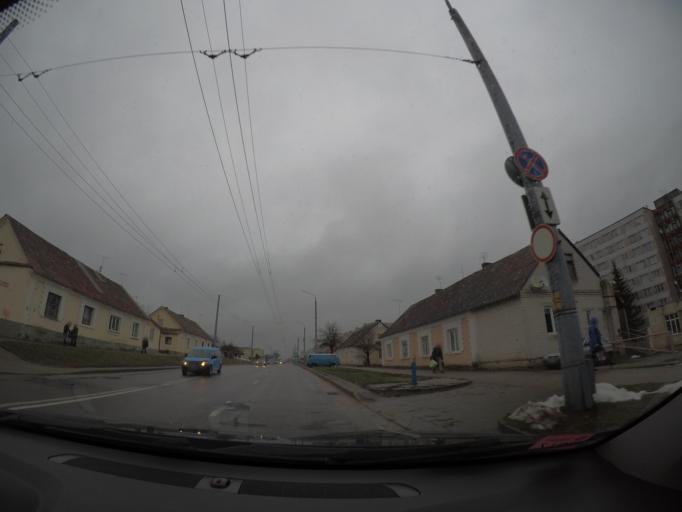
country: BY
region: Grodnenskaya
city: Hrodna
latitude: 53.6971
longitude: 23.8399
